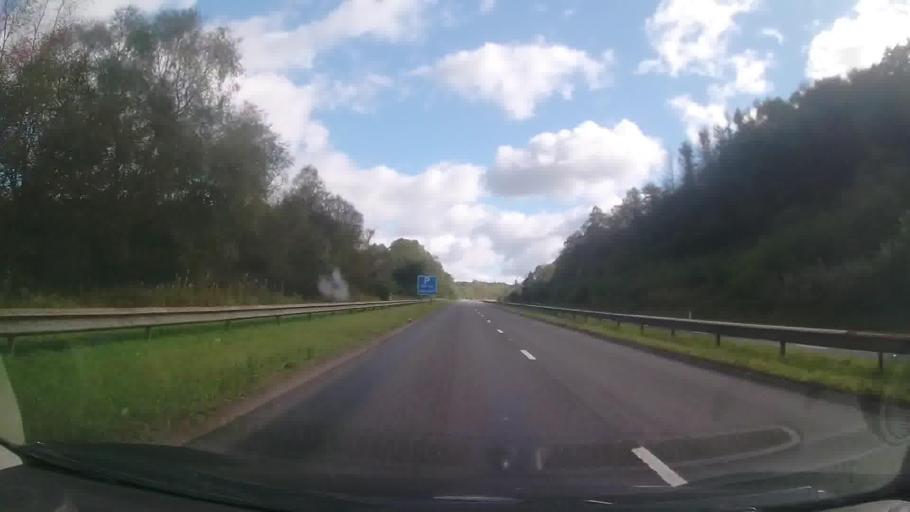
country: GB
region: Wales
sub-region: Neath Port Talbot
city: Glyn-neath
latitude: 51.7564
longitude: -3.5837
